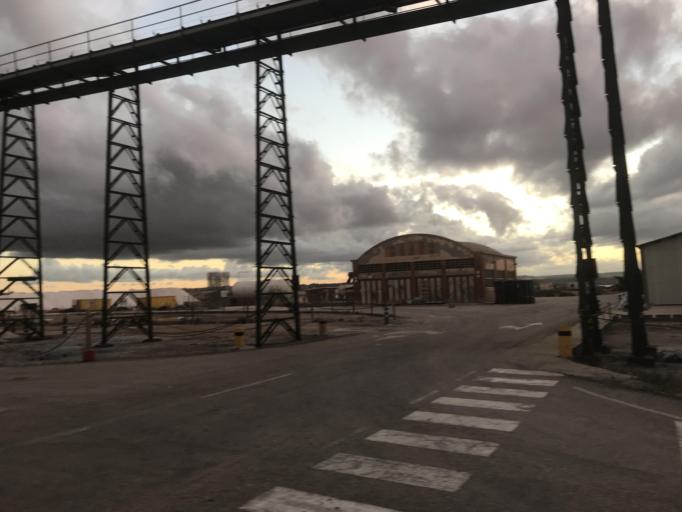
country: ES
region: Valencia
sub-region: Provincia de Alicante
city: Torrevieja
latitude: 37.9792
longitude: -0.6990
